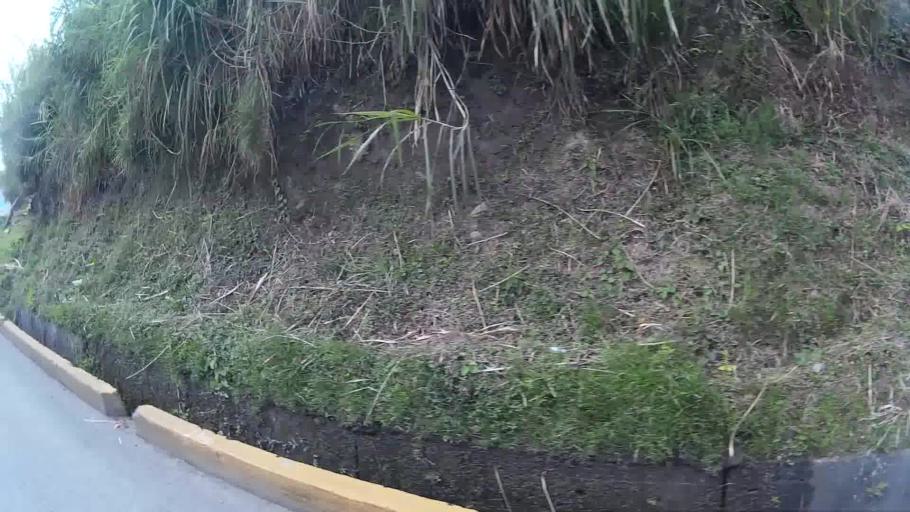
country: CO
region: Risaralda
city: Pereira
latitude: 4.8178
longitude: -75.7420
